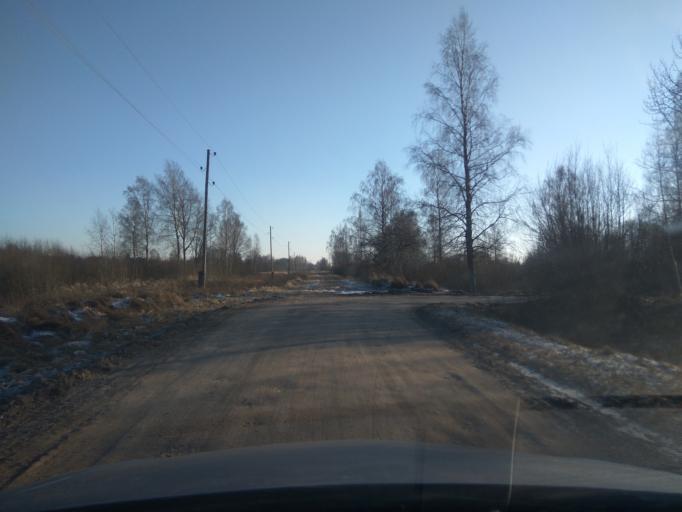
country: LV
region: Kuldigas Rajons
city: Kuldiga
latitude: 56.9633
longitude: 21.9579
